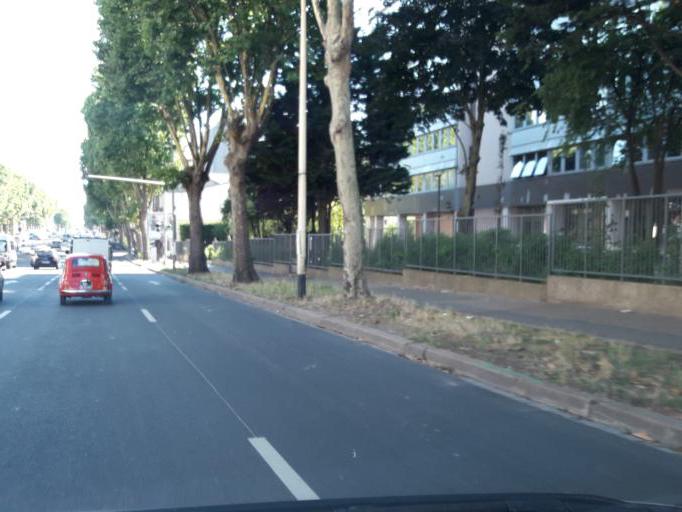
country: FR
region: Ile-de-France
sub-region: Departement du Val-de-Marne
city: Arcueil
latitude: 48.8005
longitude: 2.3234
